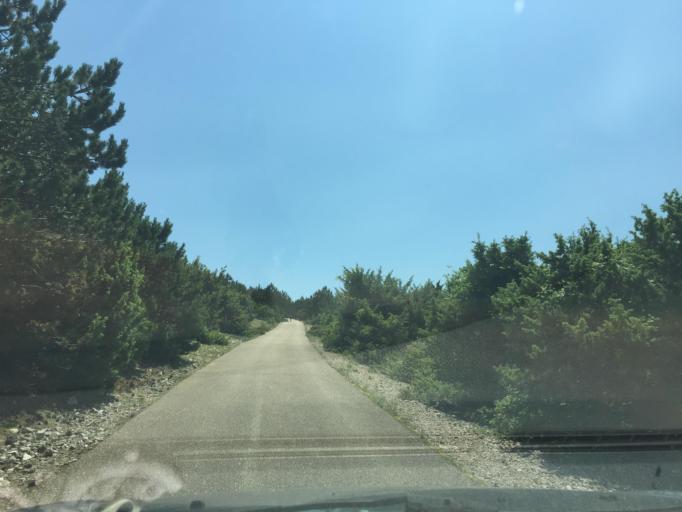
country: HR
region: Primorsko-Goranska
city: Punat
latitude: 45.0205
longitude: 14.6735
